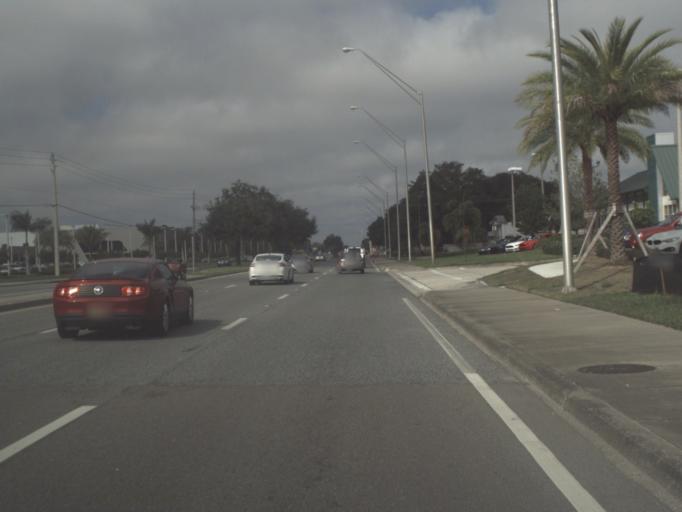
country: US
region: Florida
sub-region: Sarasota County
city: Bee Ridge
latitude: 27.2693
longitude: -82.4671
